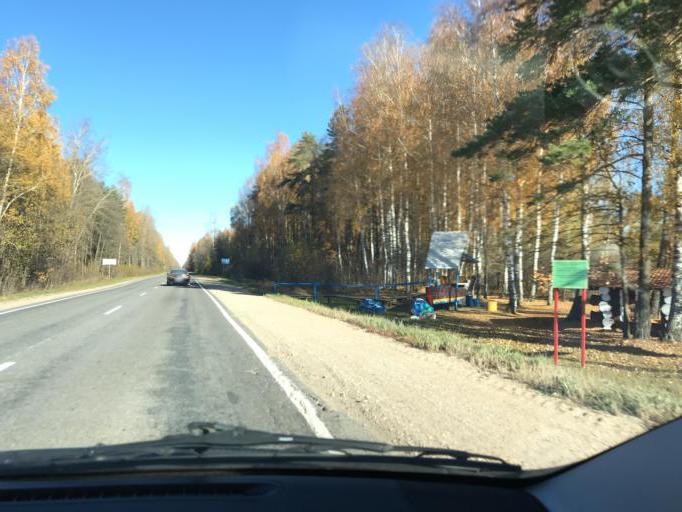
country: BY
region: Vitebsk
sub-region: Ushatski Rayon
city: Ushachy
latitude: 55.0600
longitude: 28.7526
